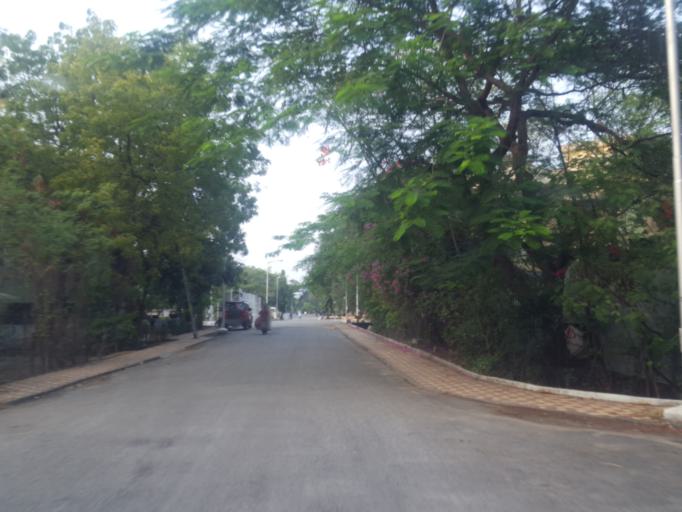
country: IN
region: Telangana
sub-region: Rangareddi
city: Singapur
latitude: 17.4681
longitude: 78.1630
